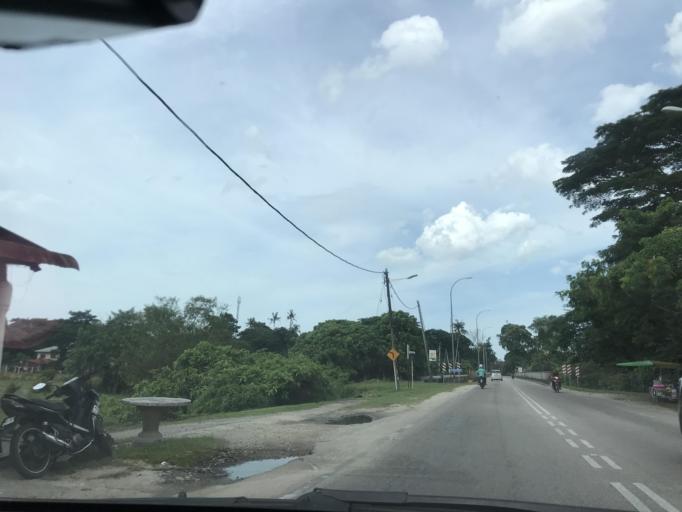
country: MY
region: Kelantan
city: Kota Bharu
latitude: 6.1026
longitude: 102.2329
